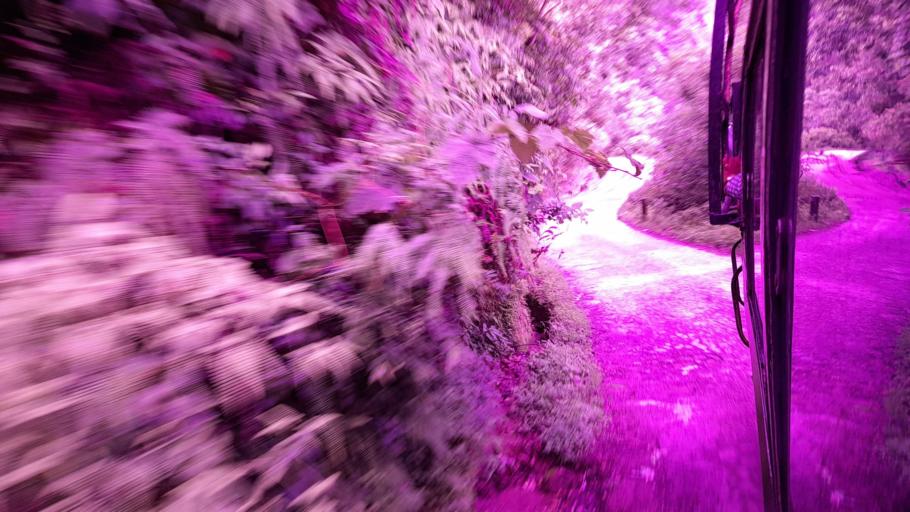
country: NP
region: Central Region
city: Kirtipur
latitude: 27.8314
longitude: 85.2074
